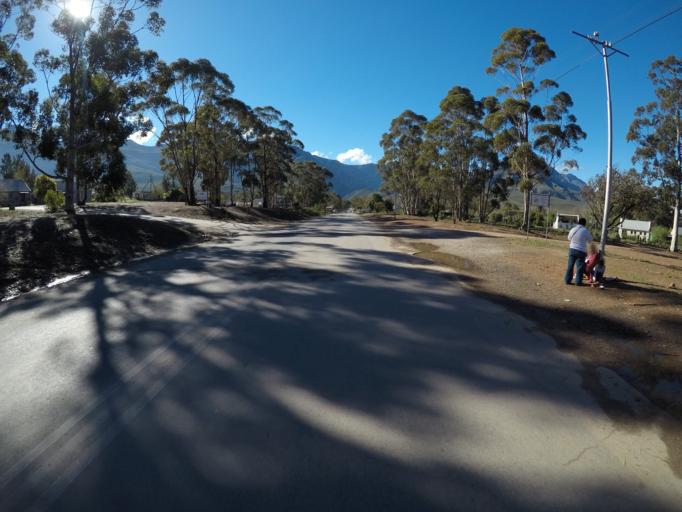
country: ZA
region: Western Cape
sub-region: Overberg District Municipality
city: Caledon
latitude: -34.0545
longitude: 19.6025
